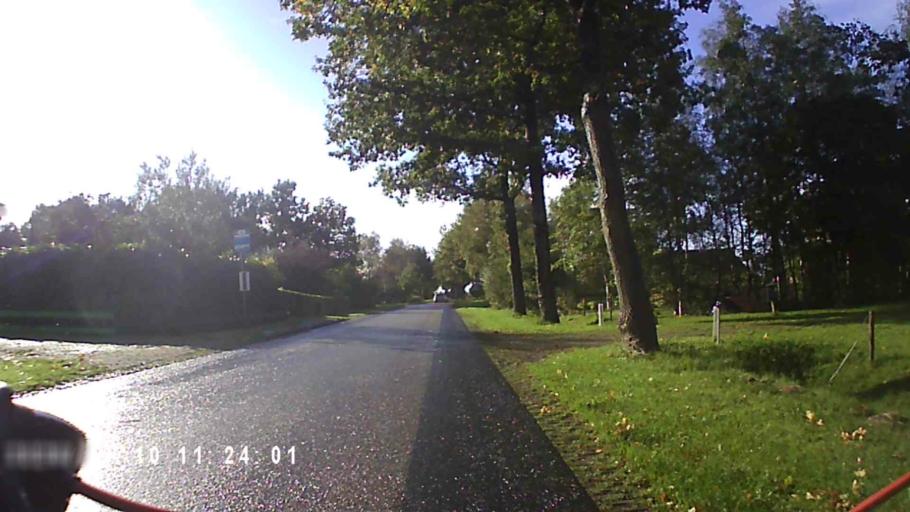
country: NL
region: Friesland
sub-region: Gemeente Smallingerland
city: Drachtstercompagnie
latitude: 53.0882
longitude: 6.1760
